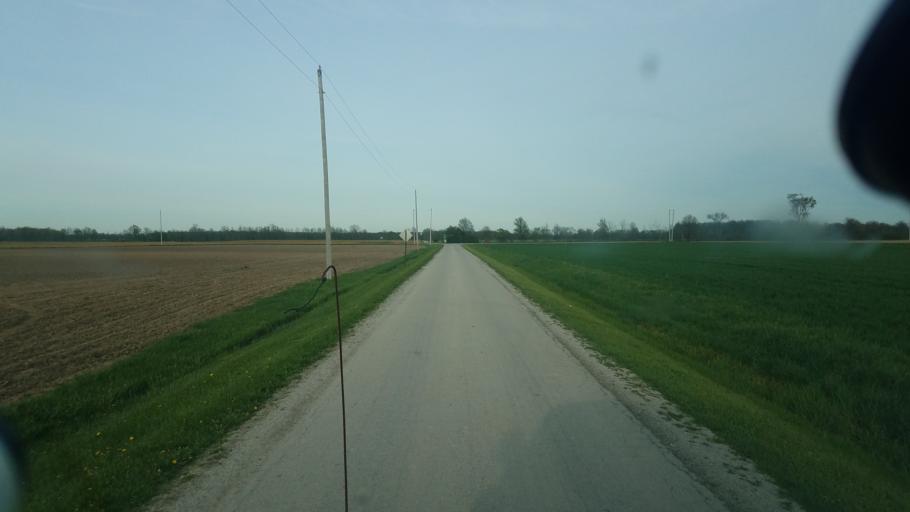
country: US
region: Ohio
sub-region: Hardin County
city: Forest
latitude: 40.7230
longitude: -83.4815
